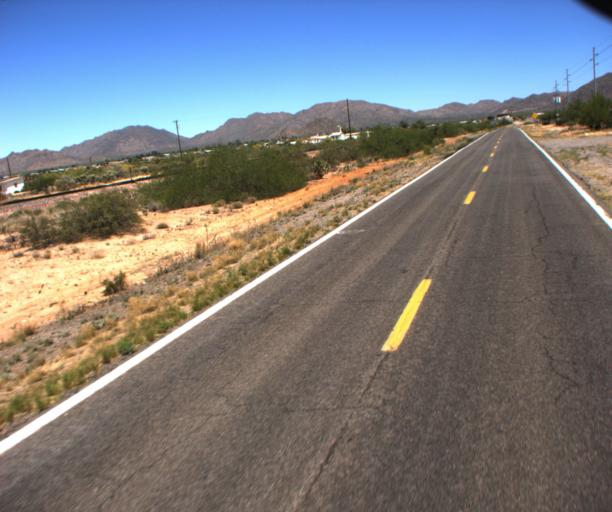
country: US
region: Arizona
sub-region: Yavapai County
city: Congress
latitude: 34.1487
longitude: -112.8429
